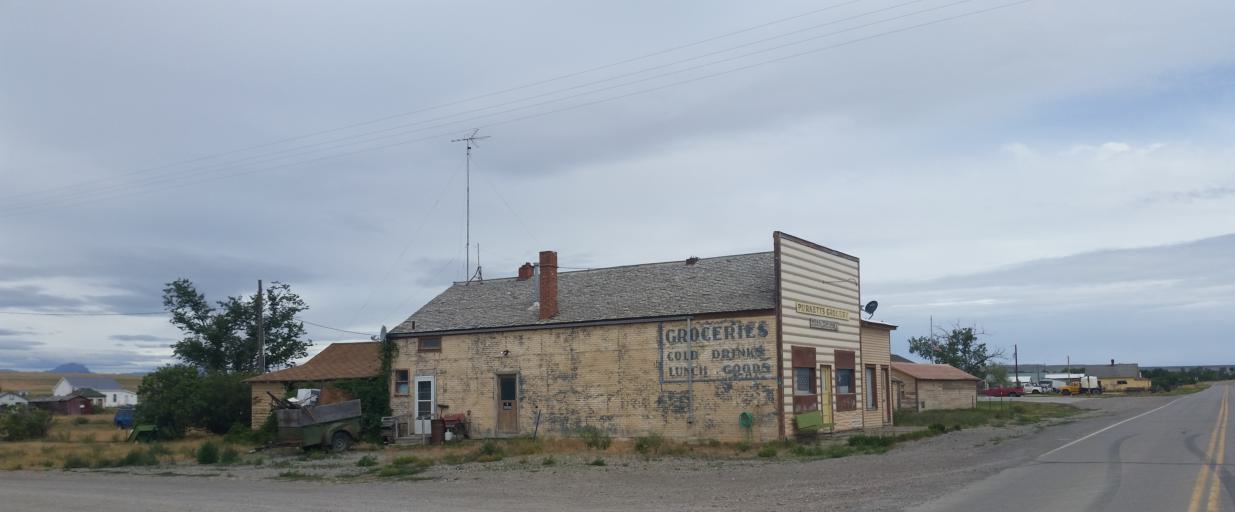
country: US
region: Montana
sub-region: Teton County
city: Choteau
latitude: 47.9772
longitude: -112.3117
